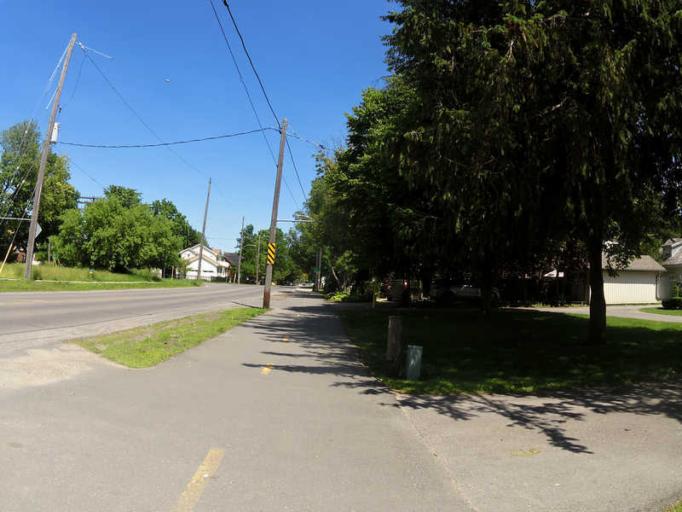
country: CA
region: Ontario
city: Peterborough
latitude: 44.3007
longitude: -78.3097
